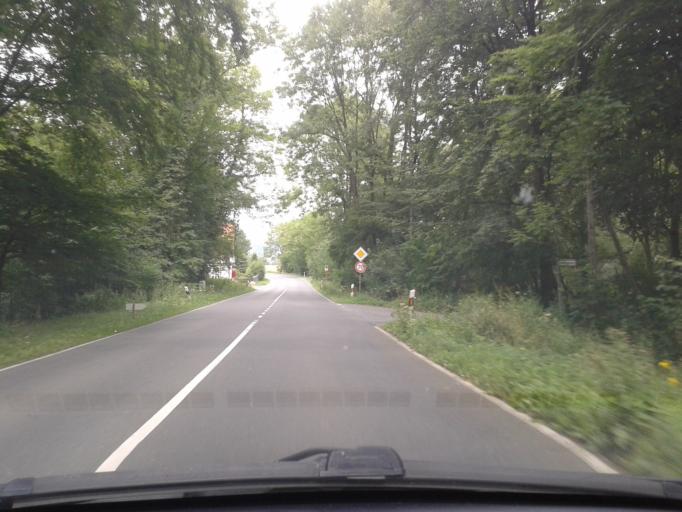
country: DE
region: North Rhine-Westphalia
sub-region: Regierungsbezirk Detmold
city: Lemgo
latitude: 52.0012
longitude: 8.9161
